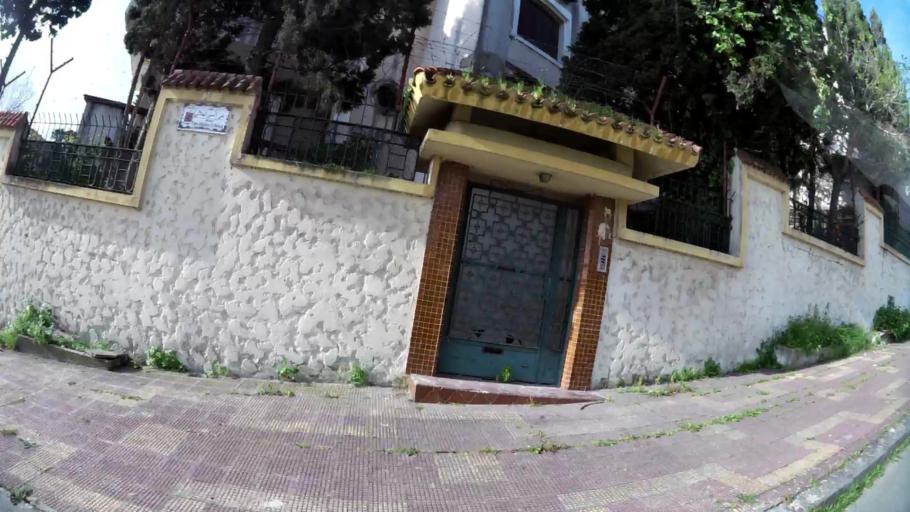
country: MA
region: Tanger-Tetouan
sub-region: Tanger-Assilah
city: Tangier
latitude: 35.7693
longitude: -5.7958
